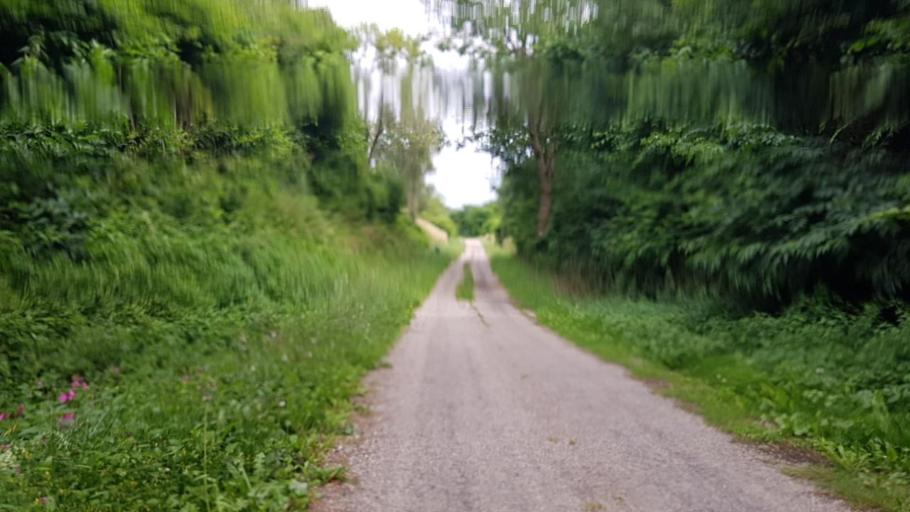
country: FR
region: Picardie
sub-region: Departement de l'Aisne
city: Origny-en-Thierache
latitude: 49.9322
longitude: 4.0091
